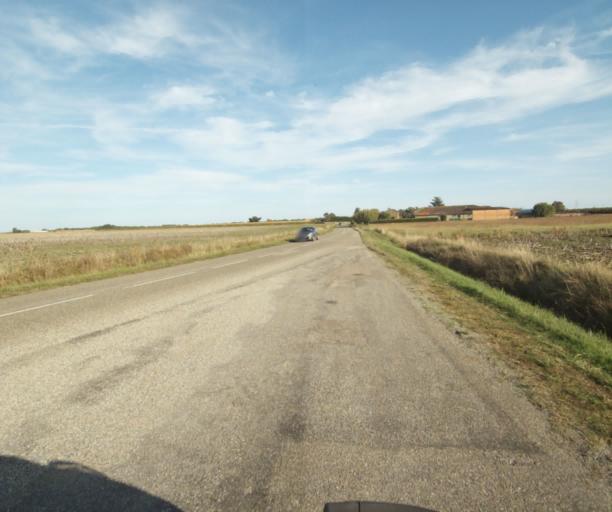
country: FR
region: Midi-Pyrenees
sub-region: Departement du Tarn-et-Garonne
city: Finhan
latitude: 43.9056
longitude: 1.1188
